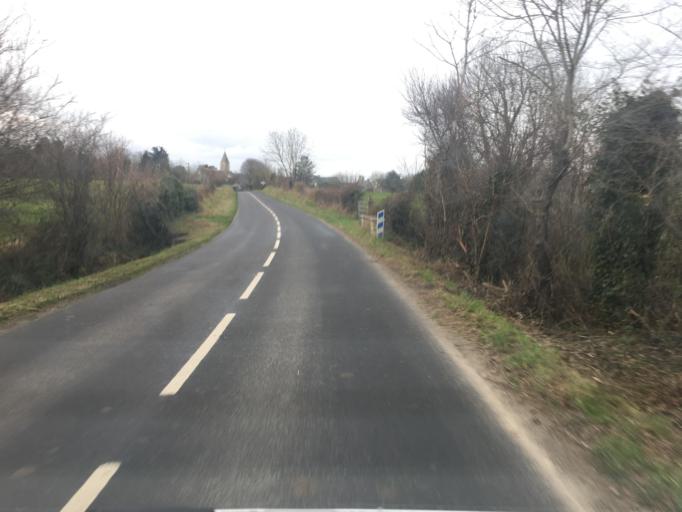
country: FR
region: Lower Normandy
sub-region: Departement du Calvados
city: Saint-Vigor-le-Grand
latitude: 49.3370
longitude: -0.6509
